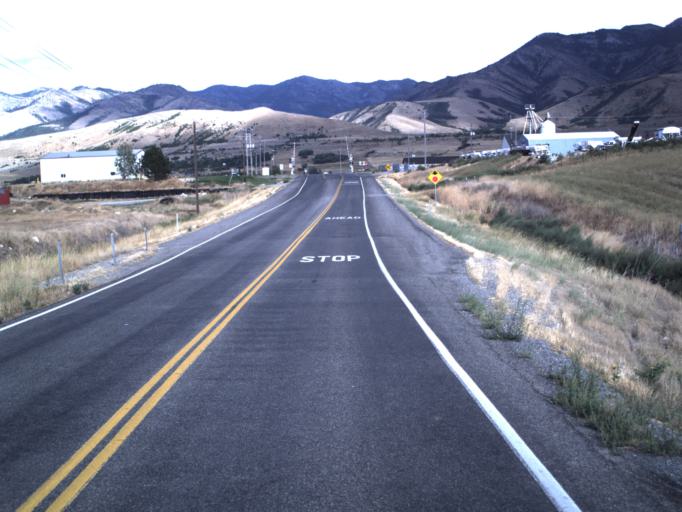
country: US
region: Utah
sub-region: Cache County
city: Lewiston
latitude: 41.9761
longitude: -111.8166
